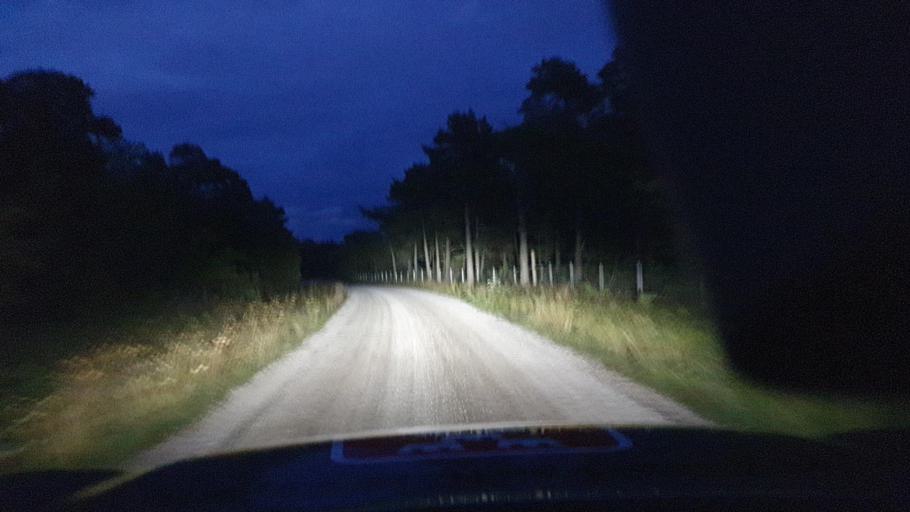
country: SE
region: Gotland
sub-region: Gotland
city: Slite
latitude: 57.8194
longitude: 18.6365
